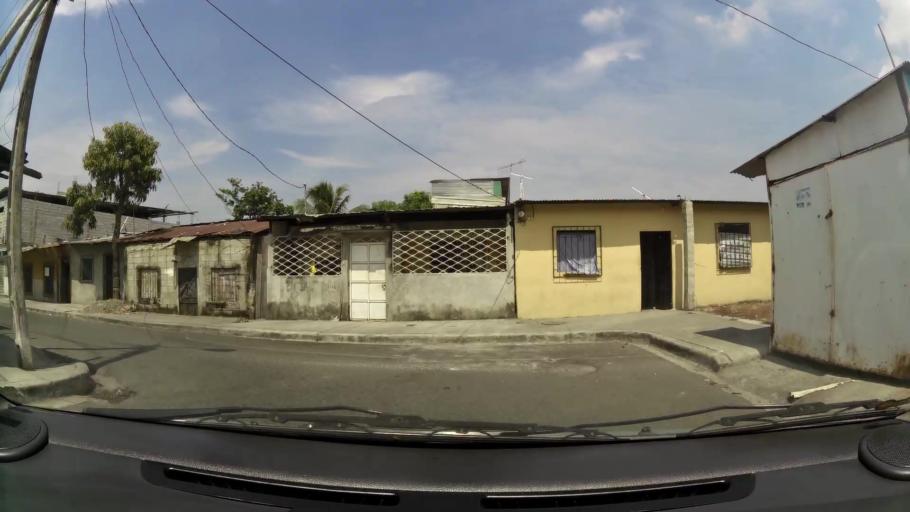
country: EC
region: Guayas
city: Guayaquil
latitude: -2.2656
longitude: -79.8731
